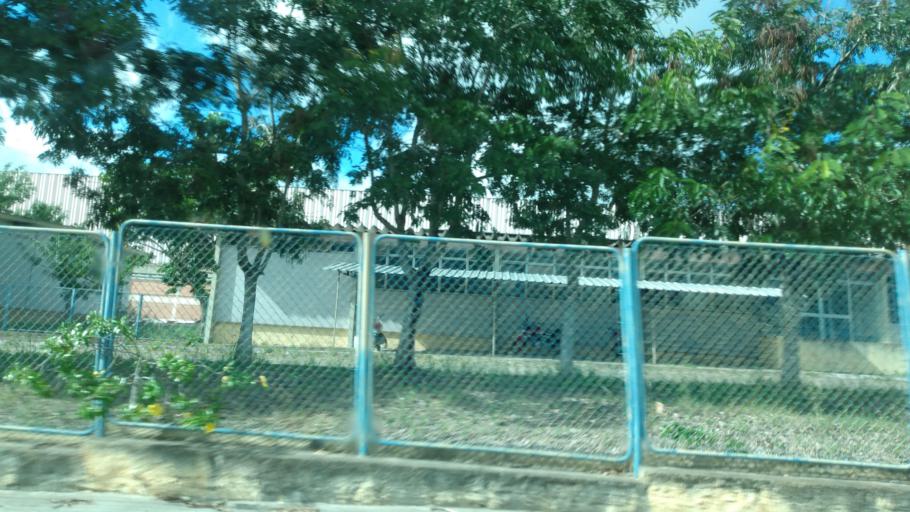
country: BR
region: Pernambuco
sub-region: Caruaru
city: Caruaru
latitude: -8.3063
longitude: -36.0150
